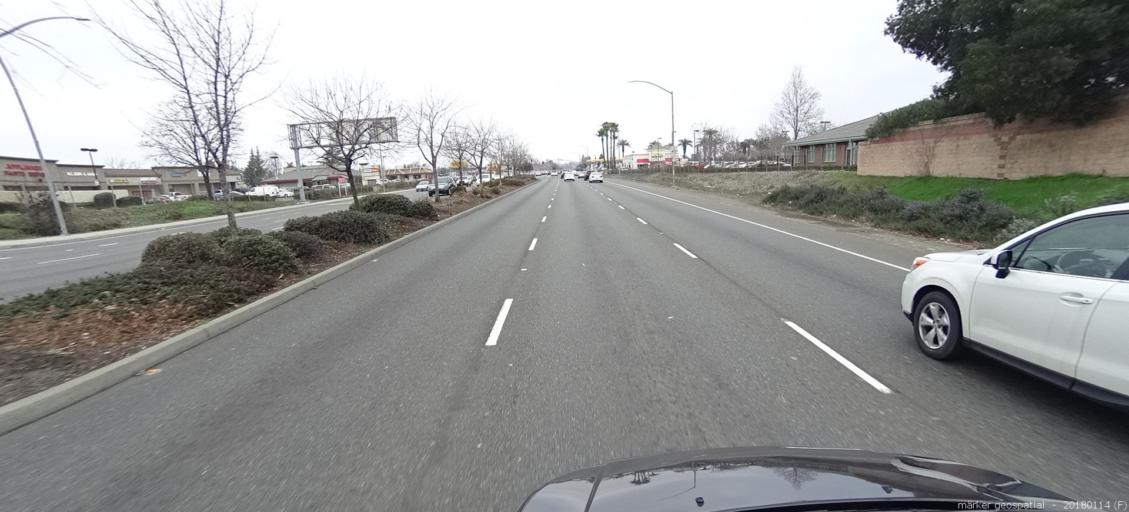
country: US
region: California
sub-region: Sacramento County
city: Gold River
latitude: 38.6132
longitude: -121.2697
